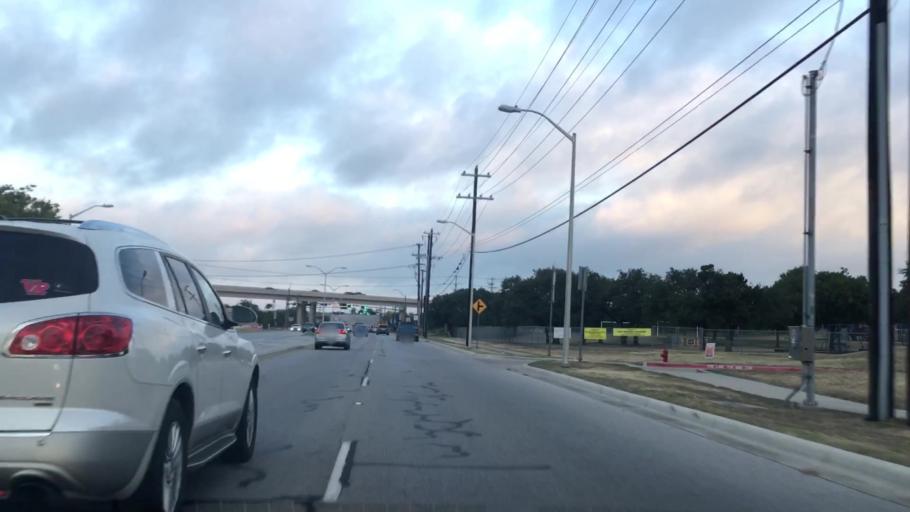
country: US
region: Texas
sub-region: Williamson County
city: Cedar Park
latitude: 30.5030
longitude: -97.8059
